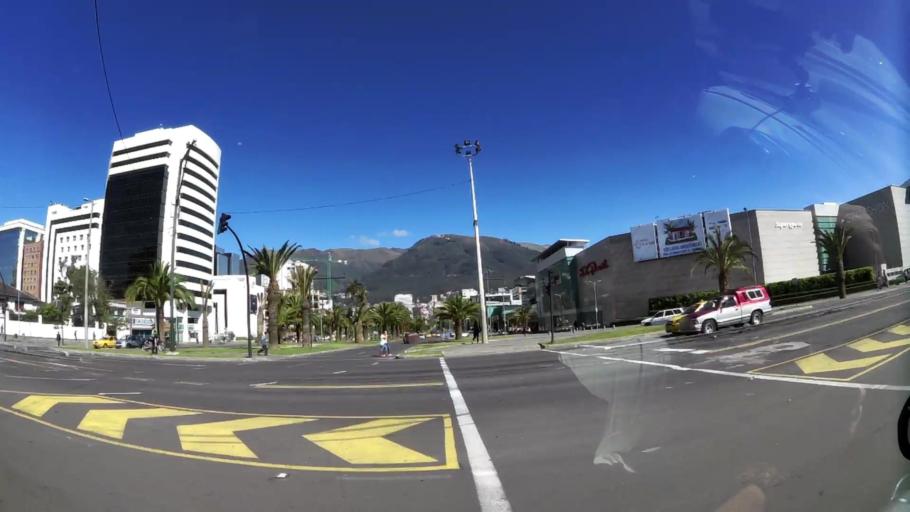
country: EC
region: Pichincha
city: Quito
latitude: -0.1770
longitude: -78.4779
